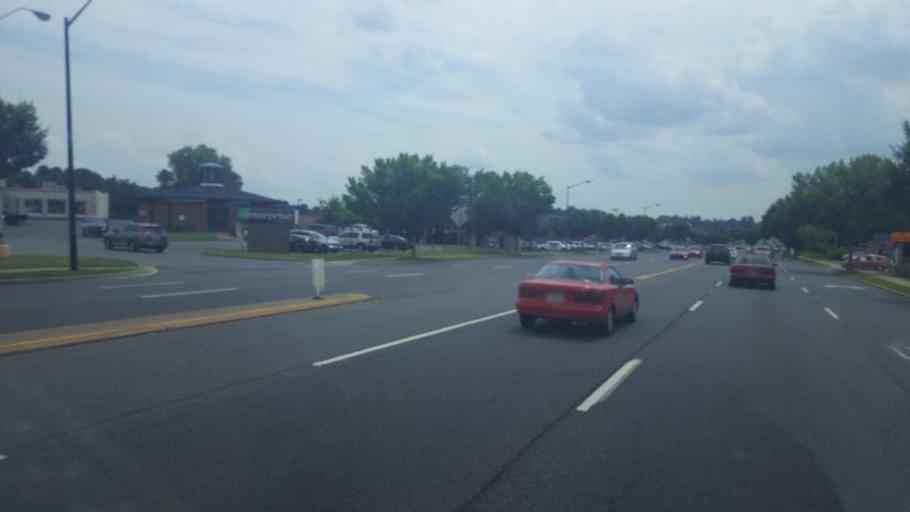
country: US
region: South Carolina
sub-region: York County
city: India Hook
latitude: 34.9674
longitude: -80.9956
